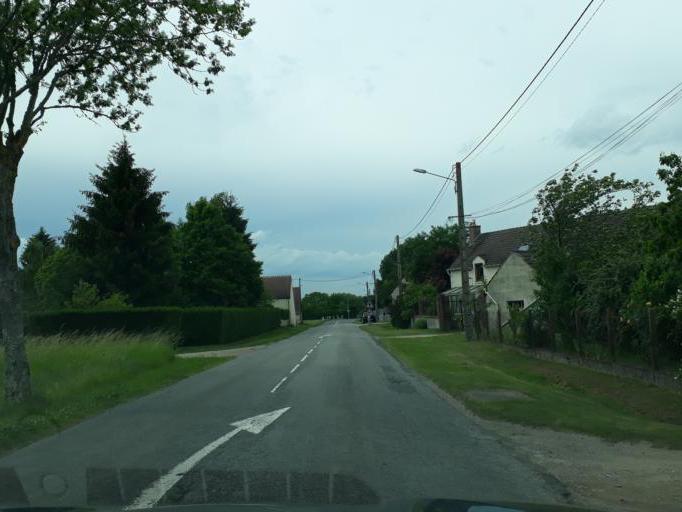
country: FR
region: Centre
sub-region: Departement du Loiret
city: Ferolles
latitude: 47.8358
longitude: 2.1408
